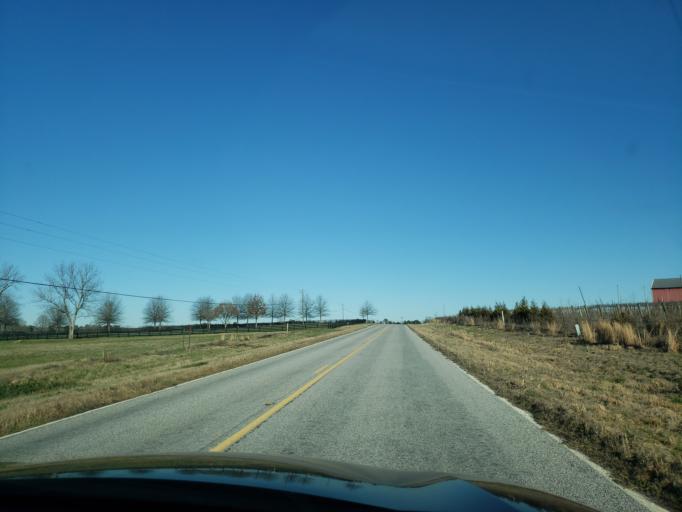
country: US
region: Alabama
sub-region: Elmore County
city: Tallassee
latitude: 32.5866
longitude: -85.7949
